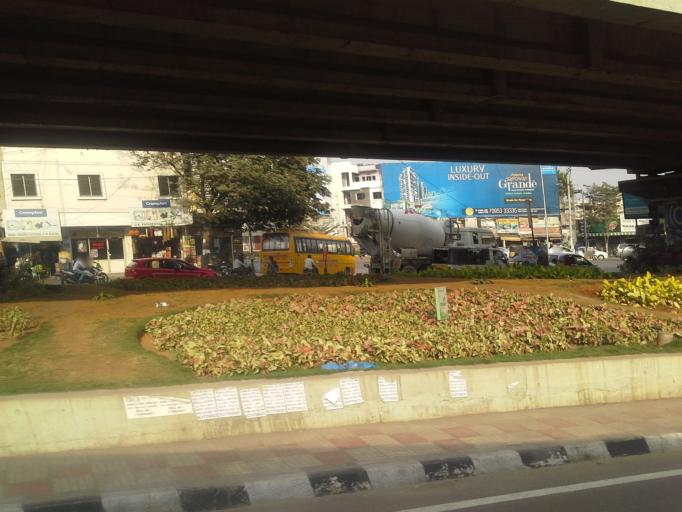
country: IN
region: Telangana
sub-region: Rangareddi
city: Kukatpalli
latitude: 17.4388
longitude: 78.3633
